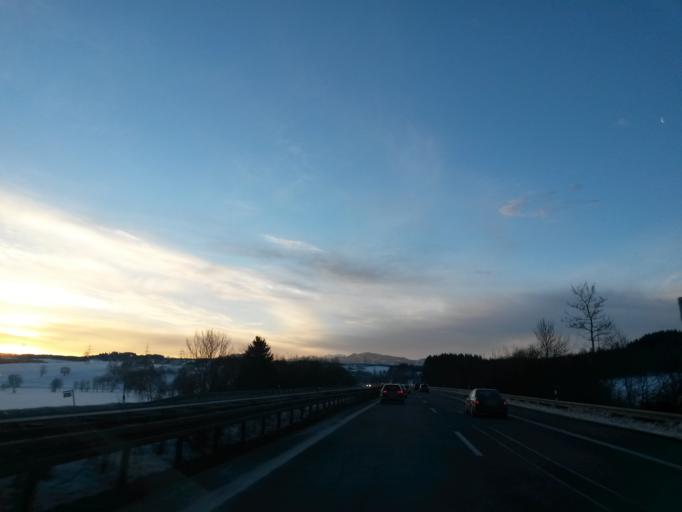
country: DE
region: Bavaria
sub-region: Swabia
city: Betzigau
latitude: 47.7306
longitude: 10.3500
